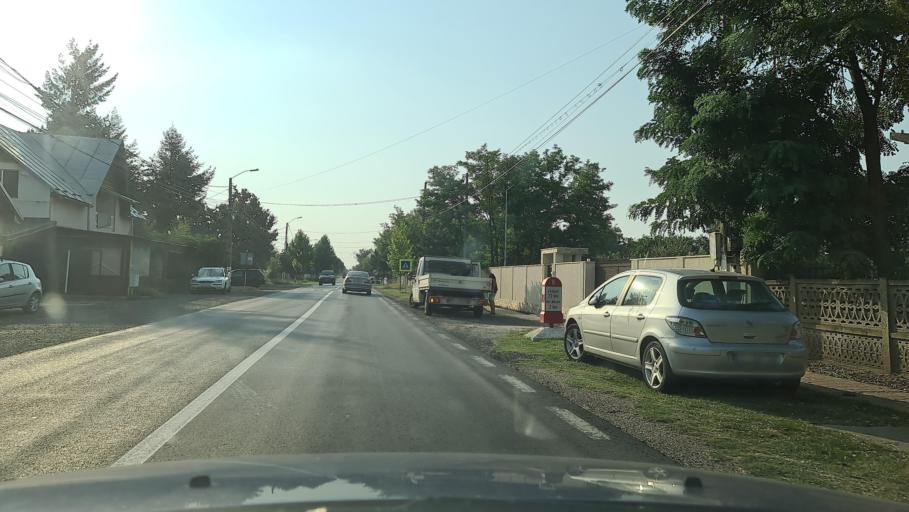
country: RO
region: Calarasi
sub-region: Comuna Dor Marunt
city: Dor Marunt
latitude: 44.4435
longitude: 26.9325
